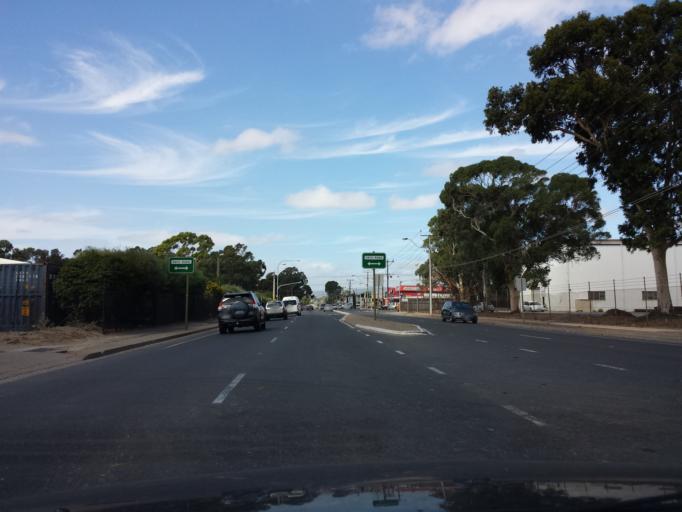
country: AU
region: South Australia
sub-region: Charles Sturt
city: Woodville
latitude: -34.8754
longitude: 138.5645
